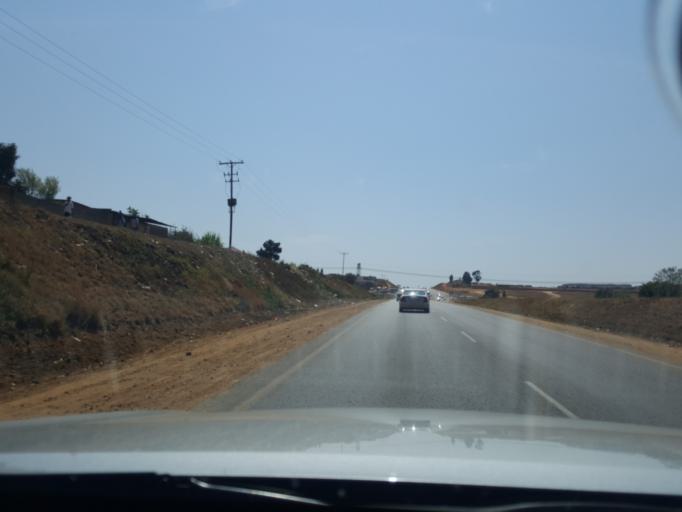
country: ZA
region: Gauteng
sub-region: City of Johannesburg Metropolitan Municipality
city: Midrand
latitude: -25.9117
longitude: 28.1007
